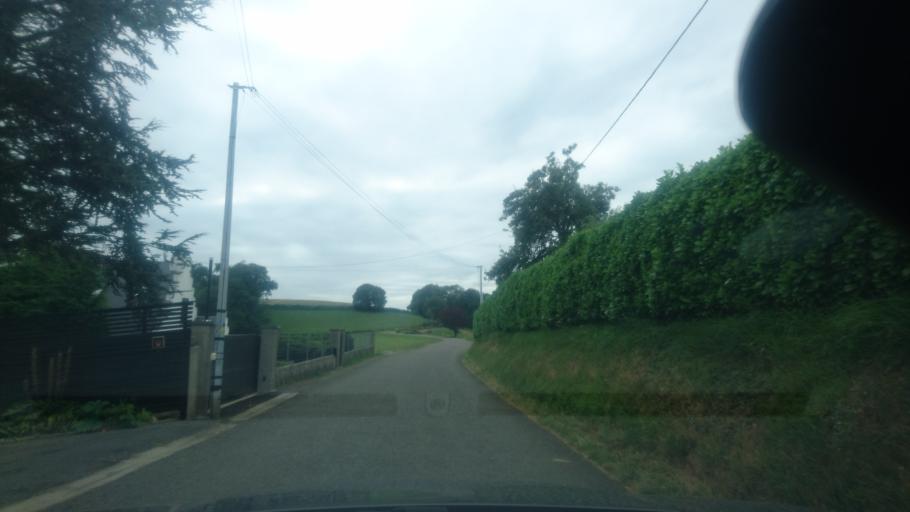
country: FR
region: Midi-Pyrenees
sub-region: Departement des Hautes-Pyrenees
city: Odos
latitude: 43.1336
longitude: 0.0562
